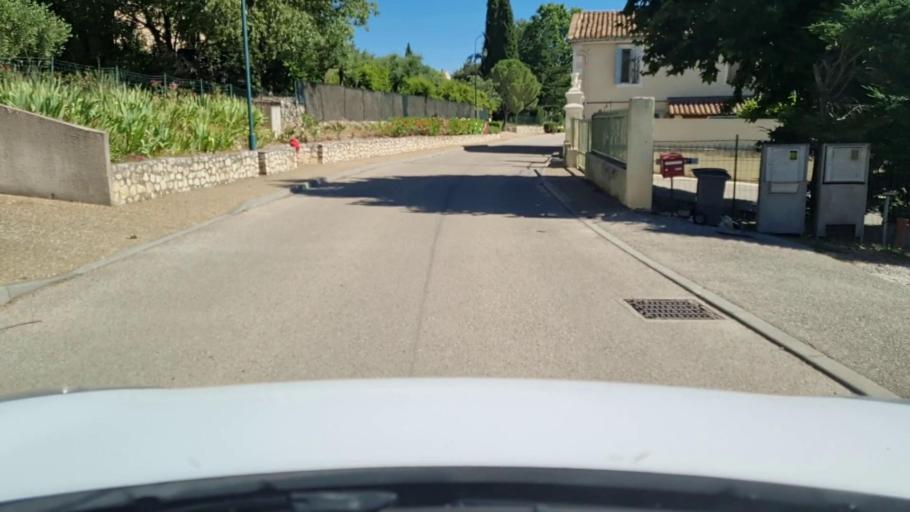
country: FR
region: Languedoc-Roussillon
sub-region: Departement du Gard
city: Villevieille
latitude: 43.8521
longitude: 4.1096
